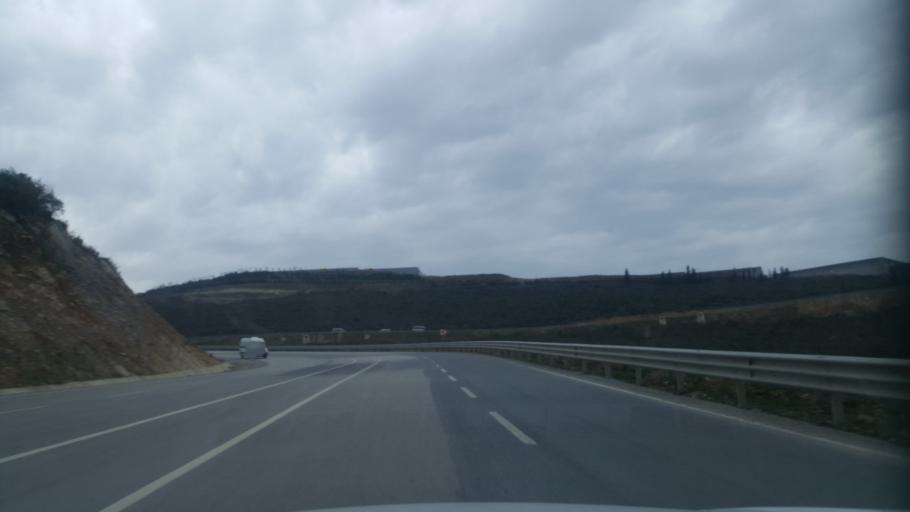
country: TR
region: Kocaeli
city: Tavsanli
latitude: 40.8417
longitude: 29.5485
